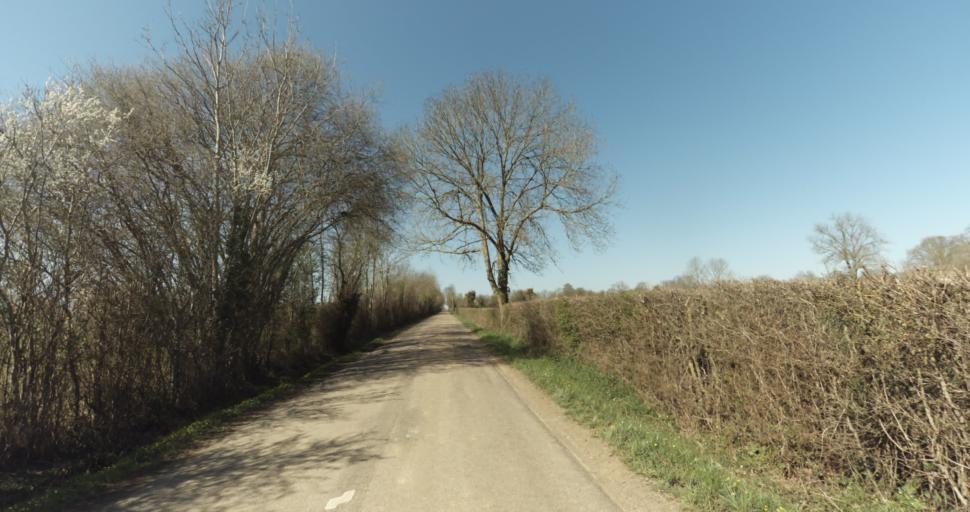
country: FR
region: Lower Normandy
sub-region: Departement du Calvados
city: Saint-Pierre-sur-Dives
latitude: 49.0013
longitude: -0.0004
